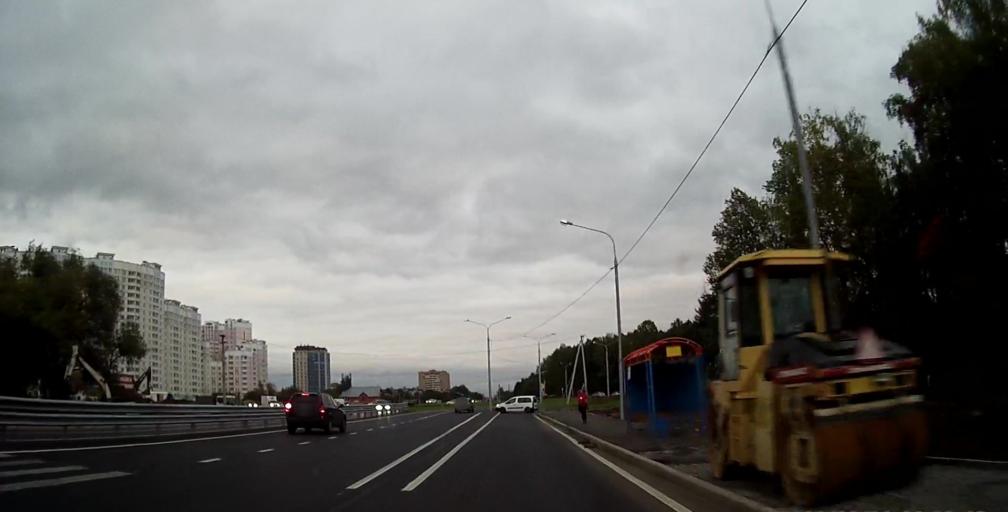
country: RU
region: Moskovskaya
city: Dubrovitsy
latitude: 55.4138
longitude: 37.4899
